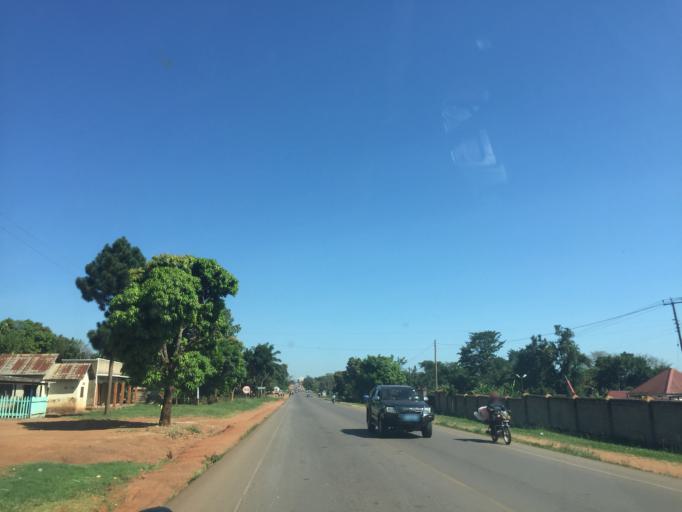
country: UG
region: Central Region
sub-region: Luwero District
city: Luwero
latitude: 0.8183
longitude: 32.5036
